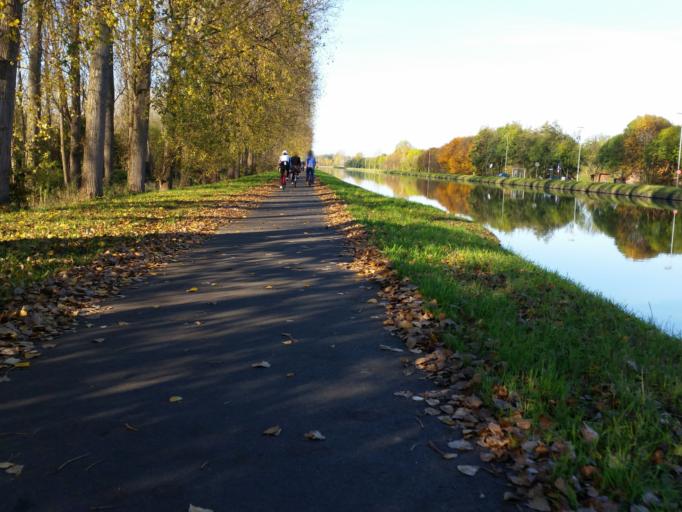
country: BE
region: Flanders
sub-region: Provincie Vlaams-Brabant
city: Leuven
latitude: 50.9084
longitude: 4.7065
